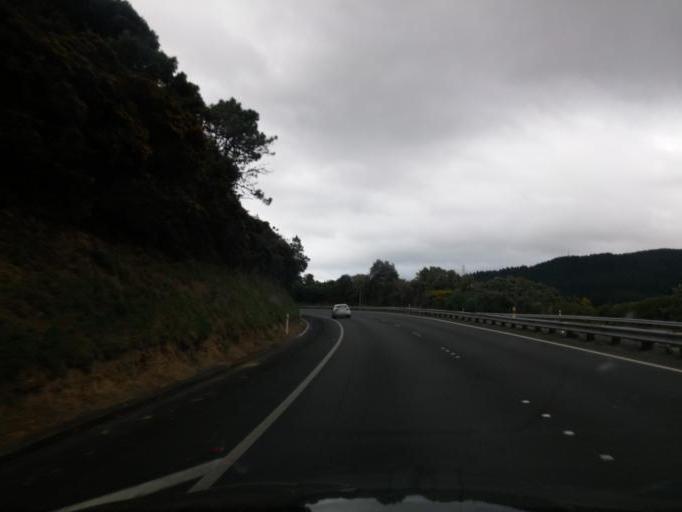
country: NZ
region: Wellington
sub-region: Porirua City
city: Porirua
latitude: -41.1799
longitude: 174.8289
